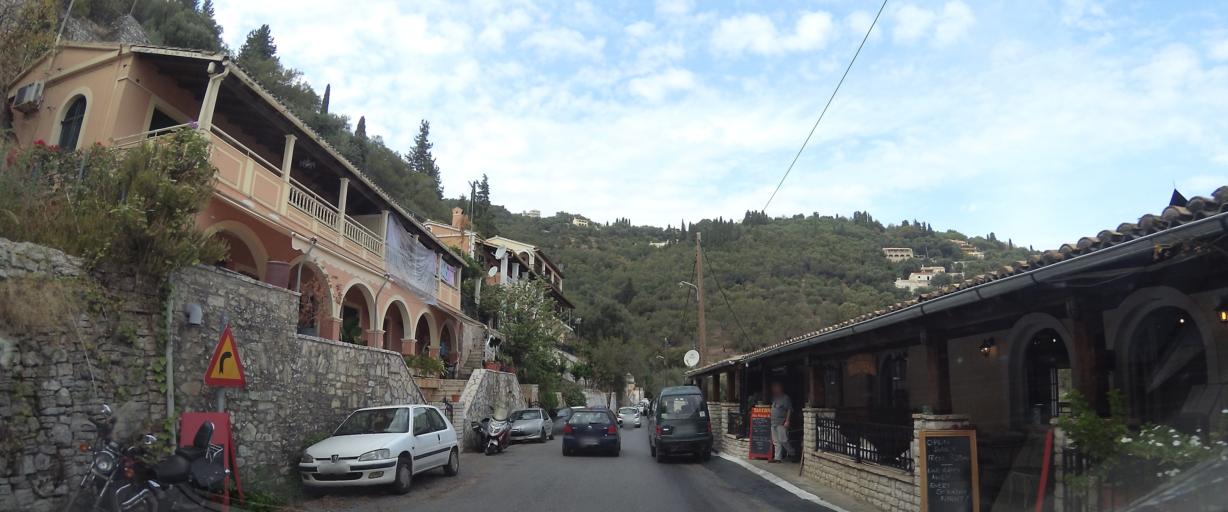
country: GR
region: Ionian Islands
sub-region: Nomos Kerkyras
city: Acharavi
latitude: 39.7450
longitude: 19.9308
